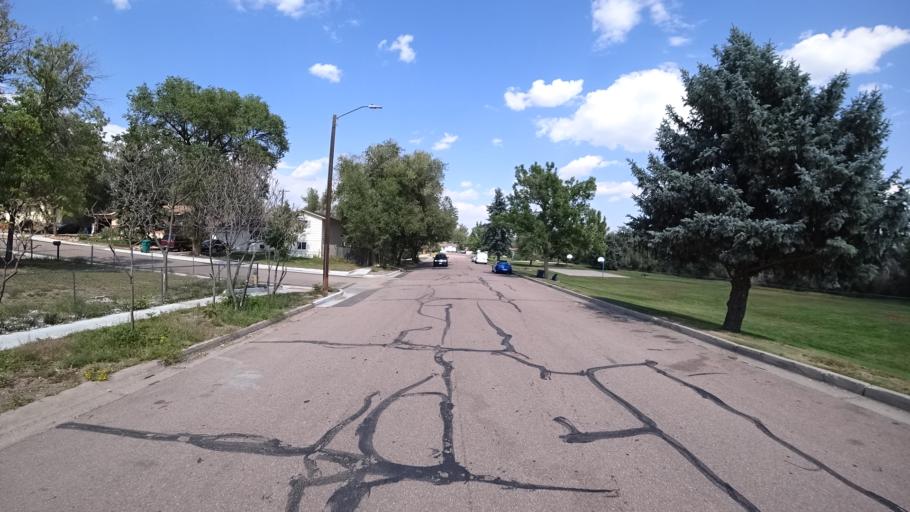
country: US
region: Colorado
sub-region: El Paso County
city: Colorado Springs
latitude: 38.8341
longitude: -104.7645
